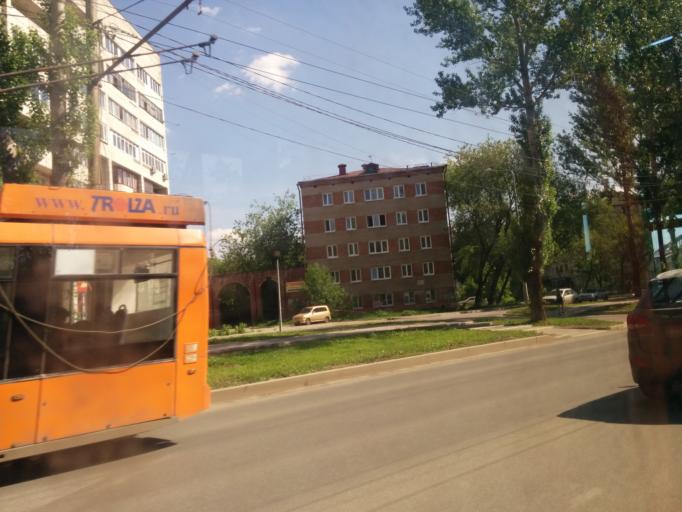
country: RU
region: Perm
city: Perm
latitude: 58.0129
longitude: 56.2804
